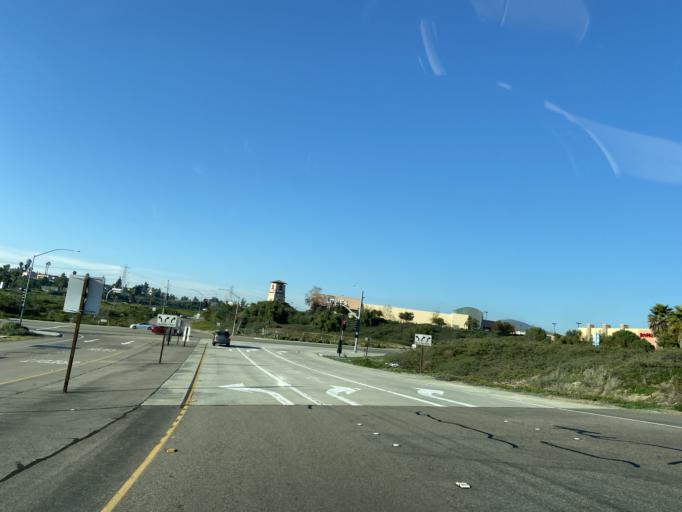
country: US
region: California
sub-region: San Diego County
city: Bonita
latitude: 32.6458
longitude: -116.9692
